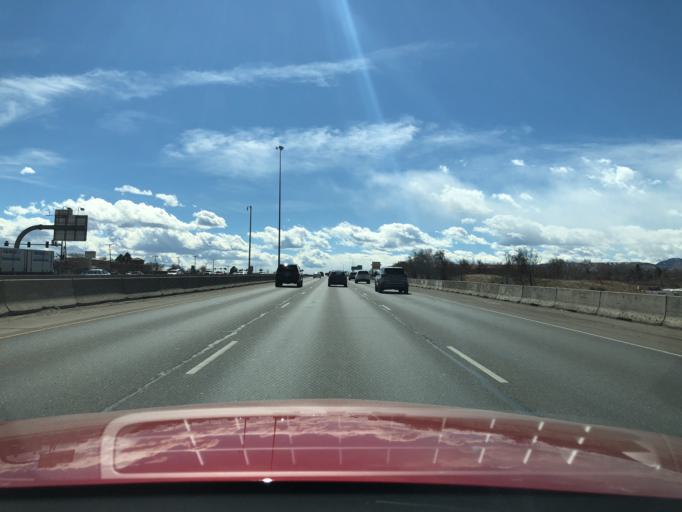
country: US
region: Colorado
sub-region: Jefferson County
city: Applewood
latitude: 39.7682
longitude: -105.1433
